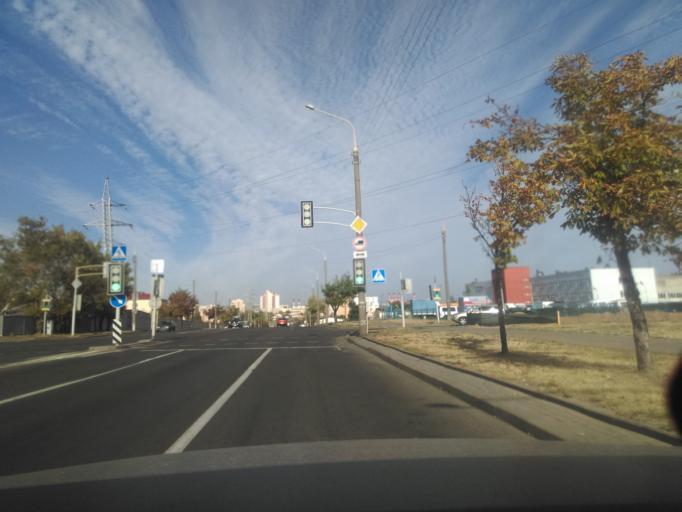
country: BY
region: Minsk
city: Minsk
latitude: 53.8778
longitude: 27.5937
